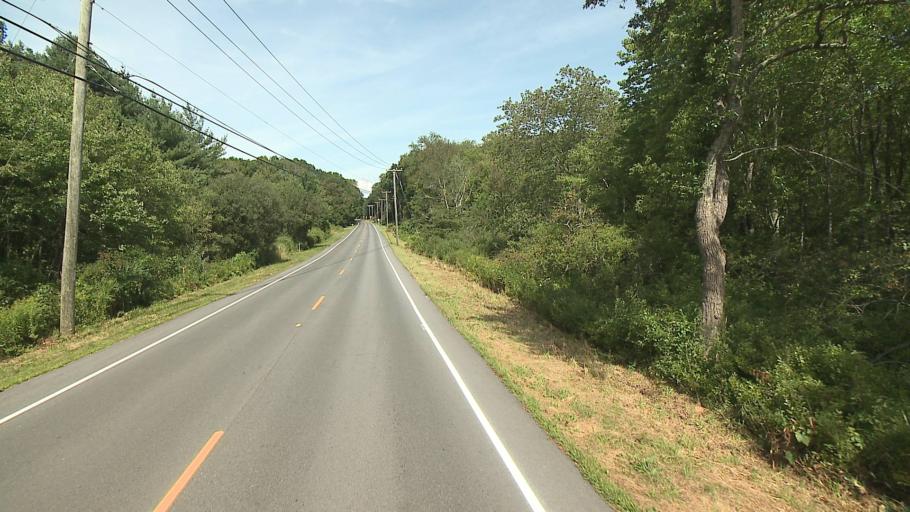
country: US
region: Connecticut
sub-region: Litchfield County
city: Bethlehem Village
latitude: 41.6268
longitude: -73.2038
